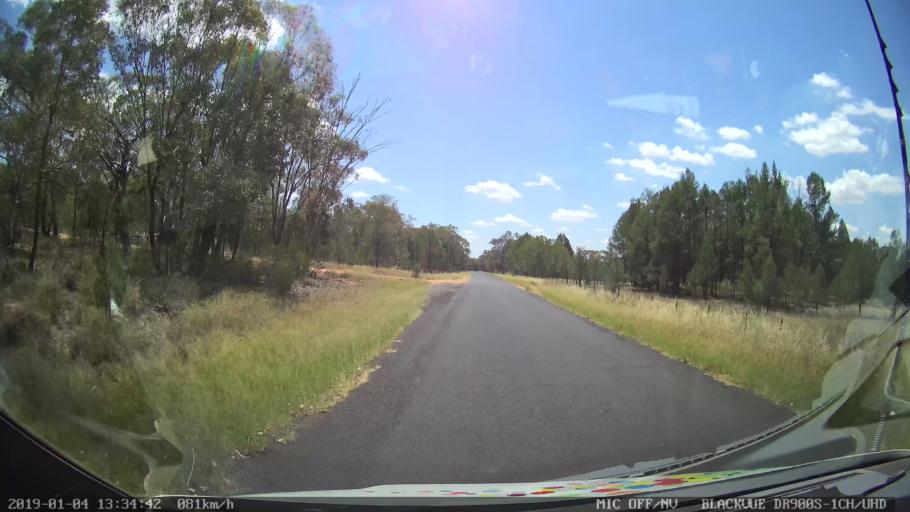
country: AU
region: New South Wales
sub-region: Dubbo Municipality
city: Dubbo
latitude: -32.5821
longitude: 148.5364
